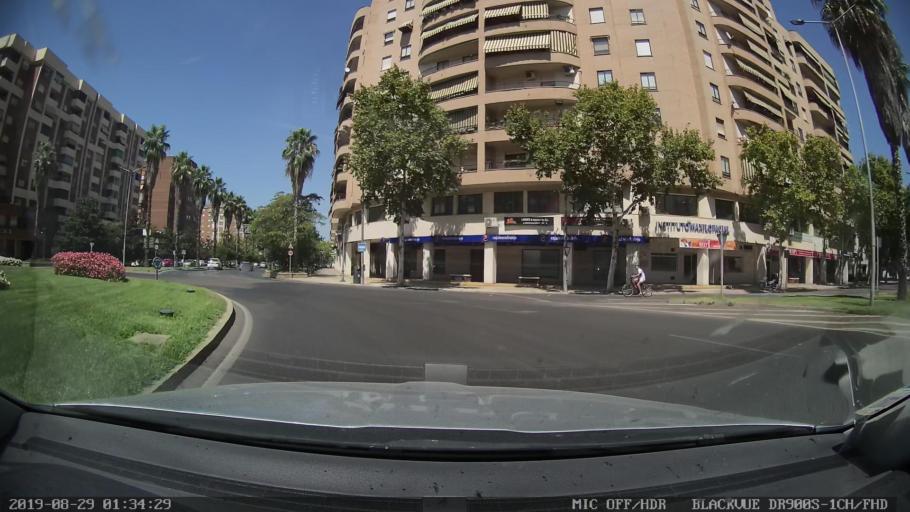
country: ES
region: Extremadura
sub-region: Provincia de Badajoz
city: Badajoz
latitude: 38.8691
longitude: -6.9879
